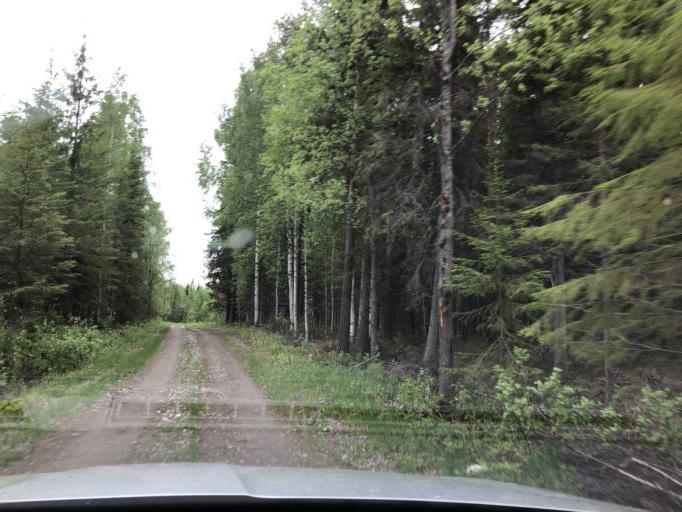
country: SE
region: Norrbotten
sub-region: Pitea Kommun
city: Roknas
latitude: 65.3984
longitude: 21.2647
